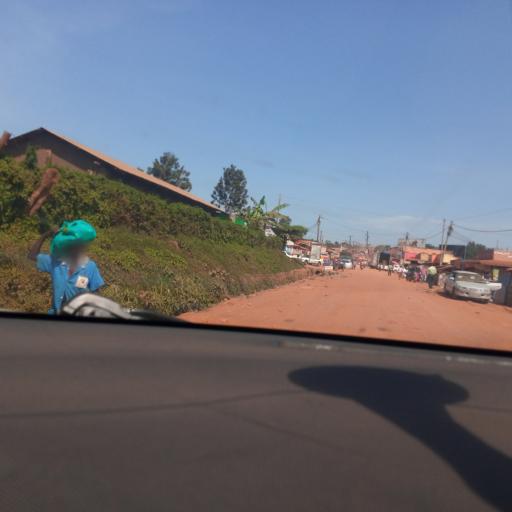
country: UG
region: Central Region
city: Masaka
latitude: -0.3159
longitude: 31.7591
